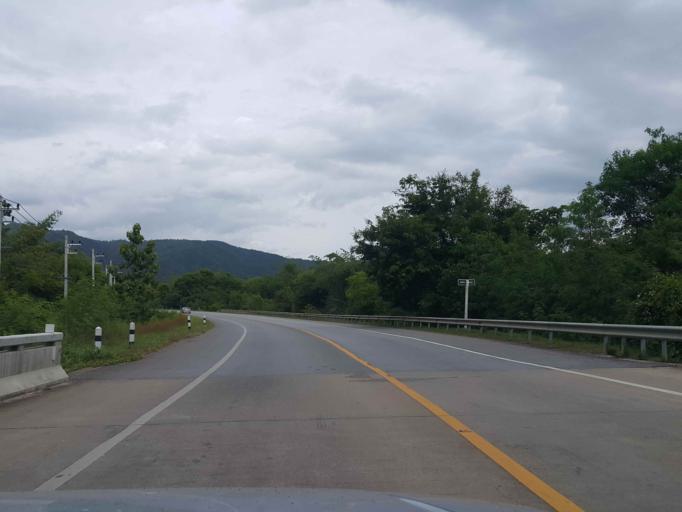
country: TH
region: Lampang
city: Lampang
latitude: 18.2511
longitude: 99.5347
